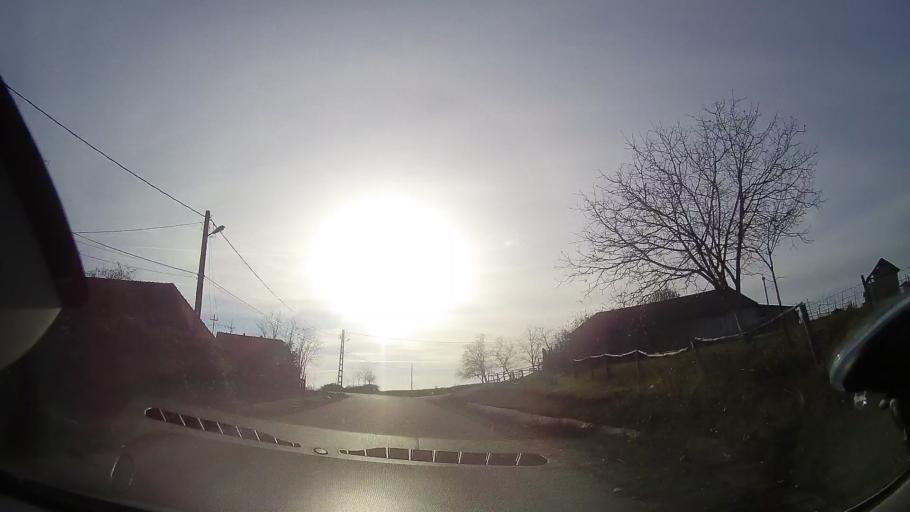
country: RO
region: Bihor
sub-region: Comuna Sarbi
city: Burzuc
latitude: 47.1212
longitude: 22.1801
